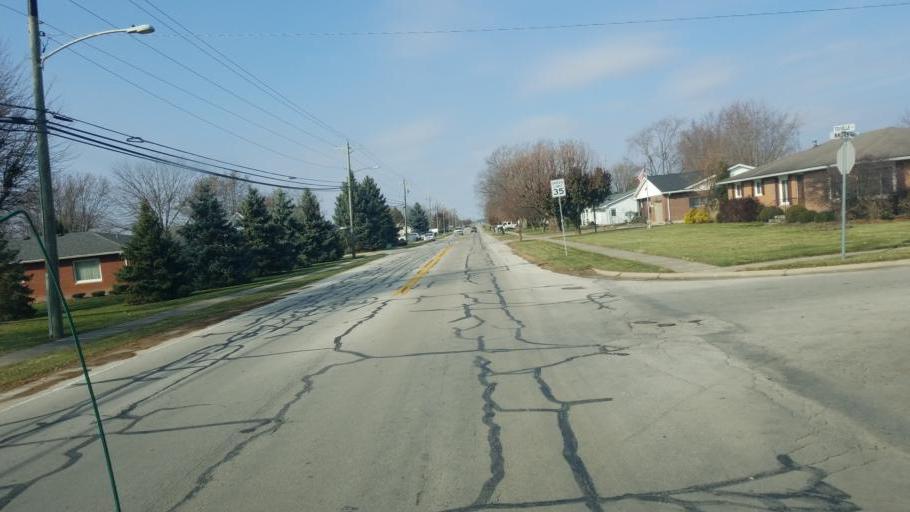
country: US
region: Ohio
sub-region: Mercer County
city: Celina
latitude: 40.5613
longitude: -84.5821
